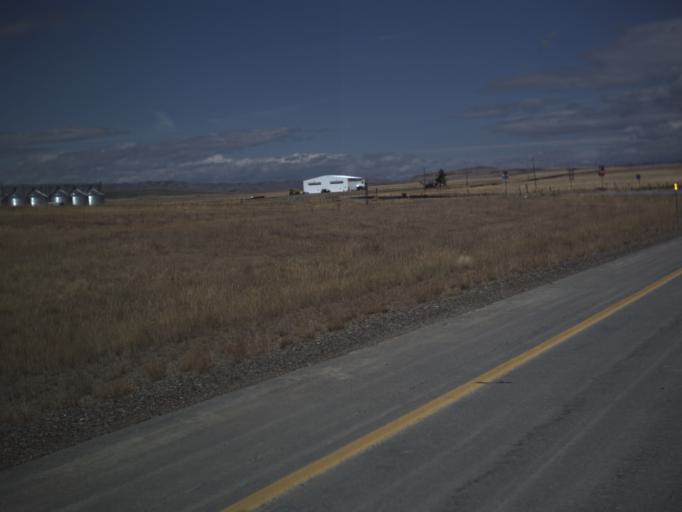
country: US
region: Utah
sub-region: Box Elder County
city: Garland
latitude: 41.8404
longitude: -112.4352
